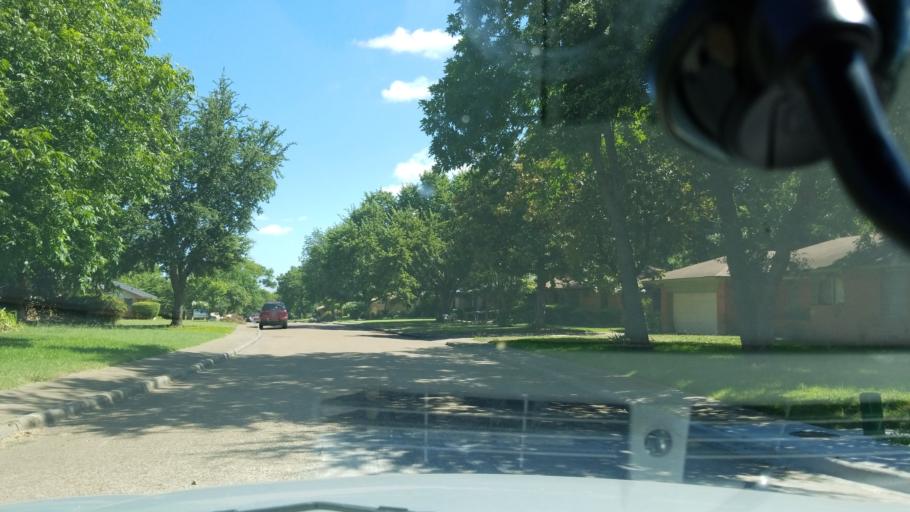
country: US
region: Texas
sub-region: Dallas County
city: Cockrell Hill
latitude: 32.6852
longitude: -96.8293
